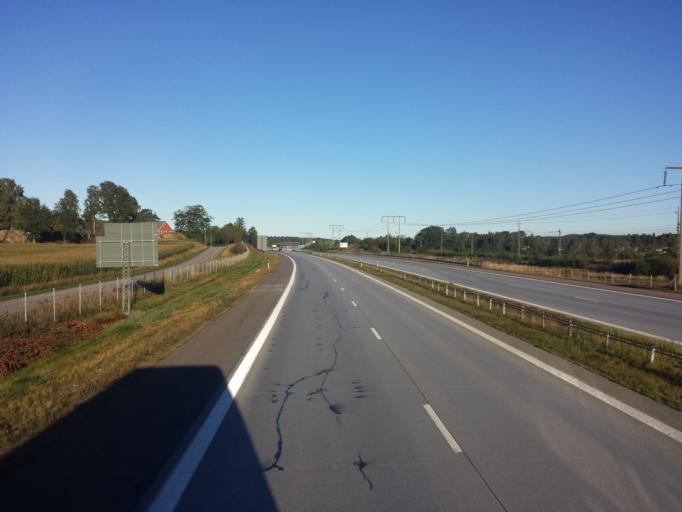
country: SE
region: Halland
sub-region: Halmstads Kommun
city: Getinge
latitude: 56.8458
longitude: 12.6927
